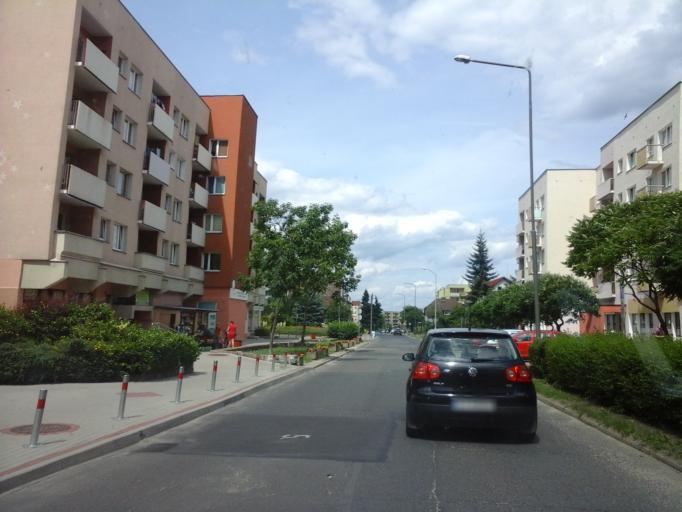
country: PL
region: West Pomeranian Voivodeship
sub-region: Szczecin
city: Szczecin
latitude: 53.3740
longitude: 14.6634
